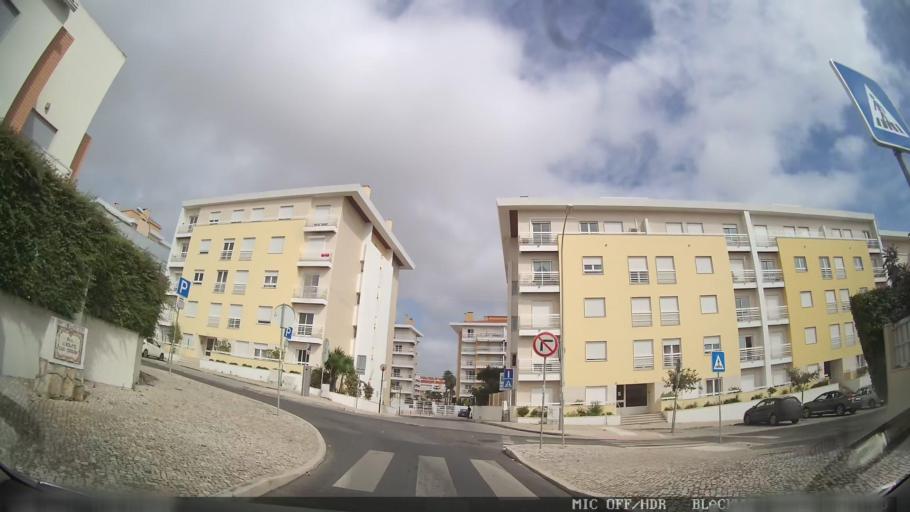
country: PT
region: Lisbon
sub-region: Cascais
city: Parede
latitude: 38.6955
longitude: -9.3690
